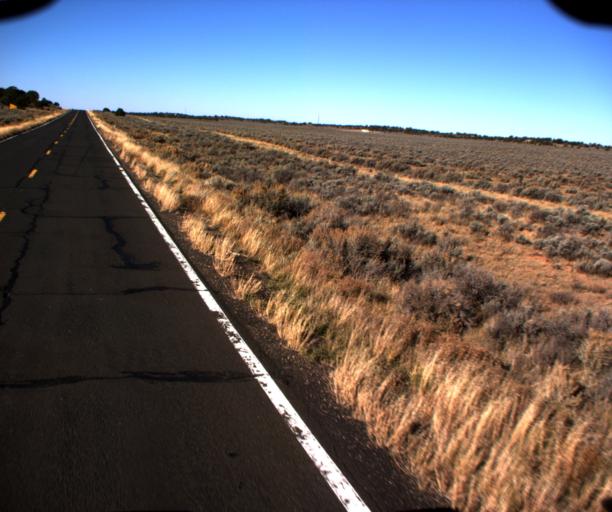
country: US
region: Arizona
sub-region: Navajo County
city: First Mesa
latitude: 35.7471
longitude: -110.0531
